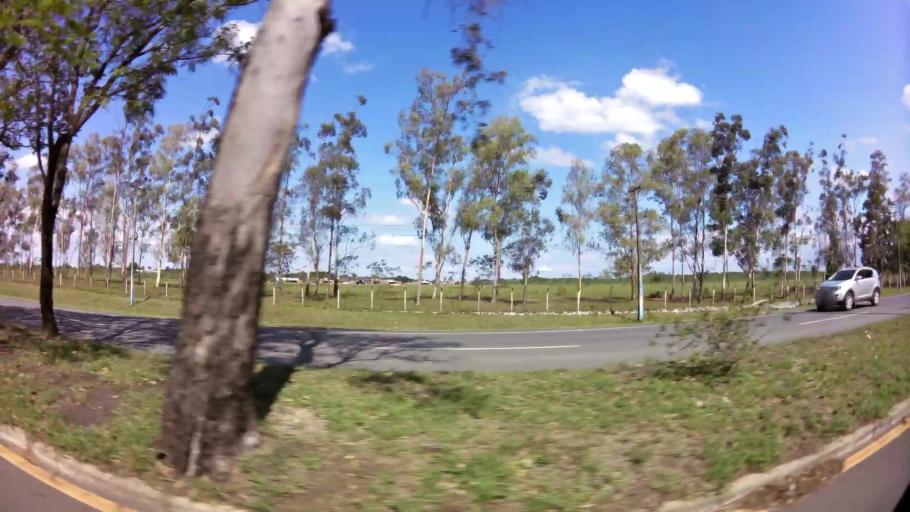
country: PY
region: Central
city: Fernando de la Mora
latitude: -25.2710
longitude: -57.5384
